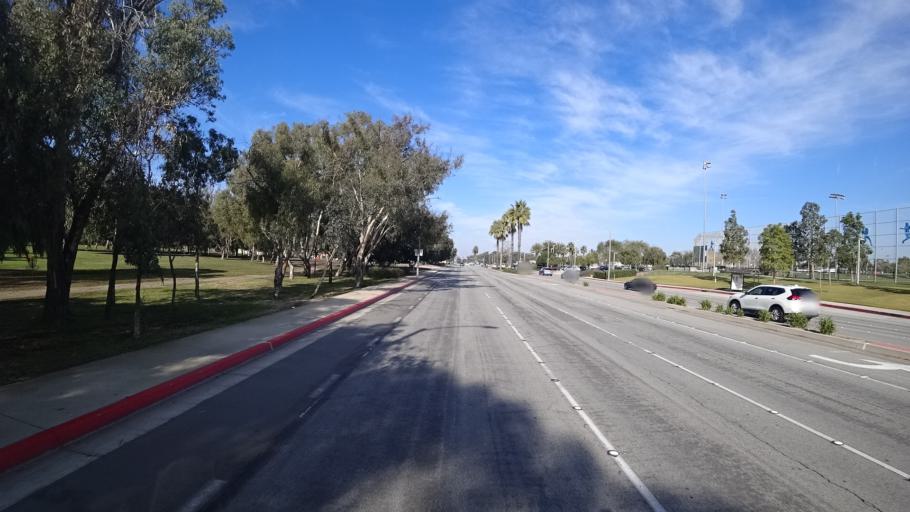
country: US
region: California
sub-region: Orange County
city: Huntington Beach
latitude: 33.6977
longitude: -118.0065
